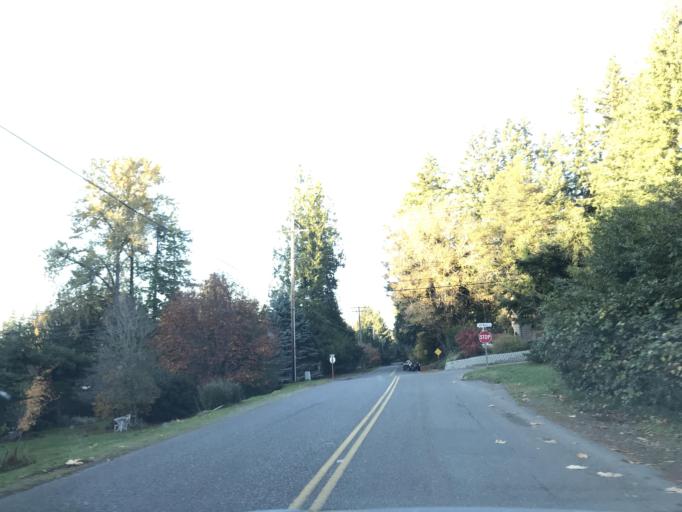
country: US
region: Washington
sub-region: Whatcom County
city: Geneva
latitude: 48.7456
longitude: -122.4153
